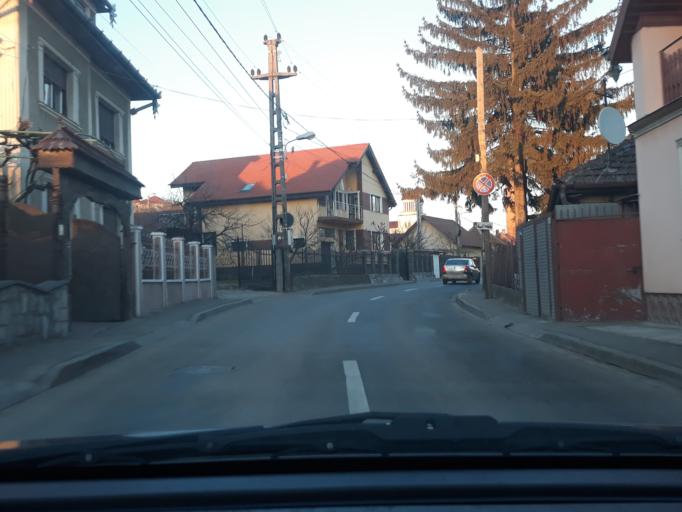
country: RO
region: Bihor
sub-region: Comuna Biharea
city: Oradea
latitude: 47.0773
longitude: 21.9384
